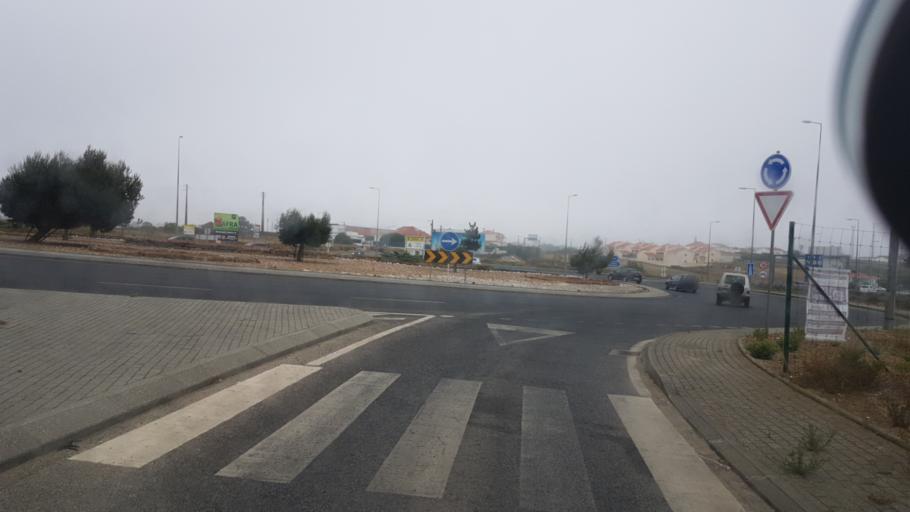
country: PT
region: Lisbon
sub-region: Mafra
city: Ericeira
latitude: 38.9650
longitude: -9.4062
